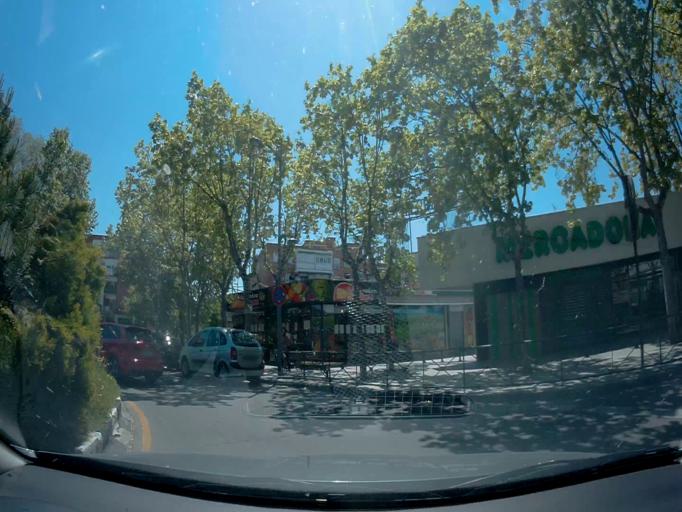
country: ES
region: Madrid
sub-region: Provincia de Madrid
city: Alcorcon
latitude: 40.3425
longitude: -3.8278
